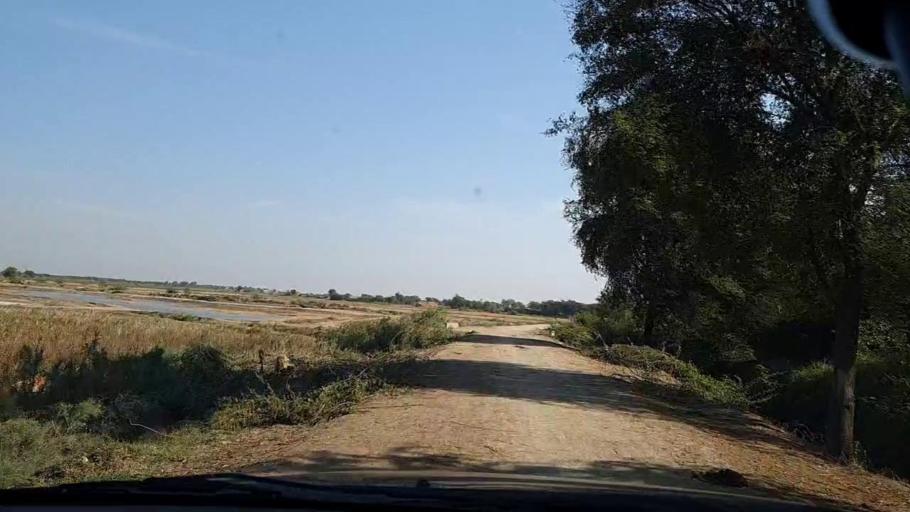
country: PK
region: Sindh
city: Mirpur Batoro
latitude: 24.6330
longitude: 68.2625
